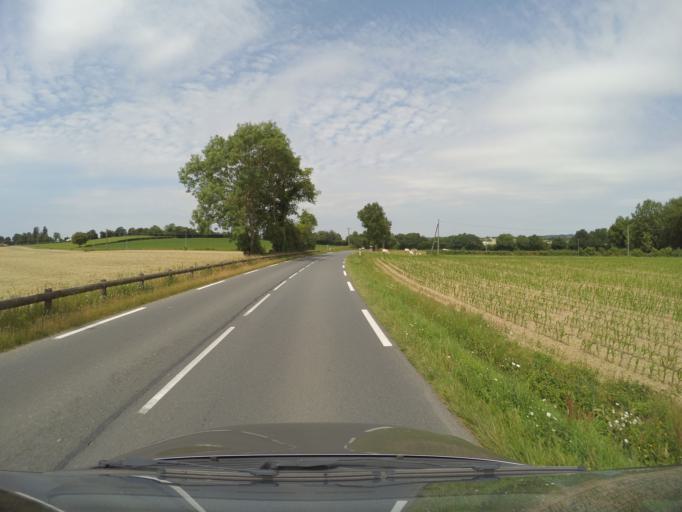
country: FR
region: Pays de la Loire
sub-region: Departement de la Vendee
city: Saint-Paul-en-Pareds
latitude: 46.8505
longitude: -0.9514
